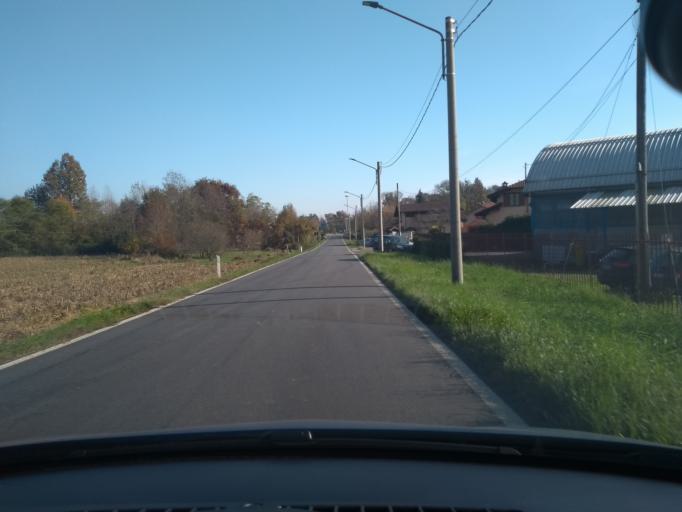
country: IT
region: Piedmont
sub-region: Provincia di Torino
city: Fiano
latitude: 45.2139
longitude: 7.5401
